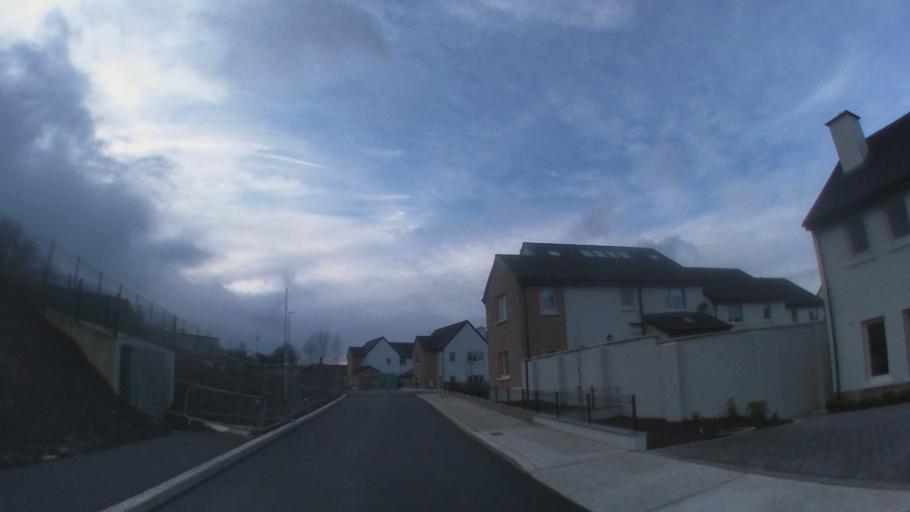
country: IE
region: Leinster
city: Donaghmede
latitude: 53.4238
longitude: -6.1721
